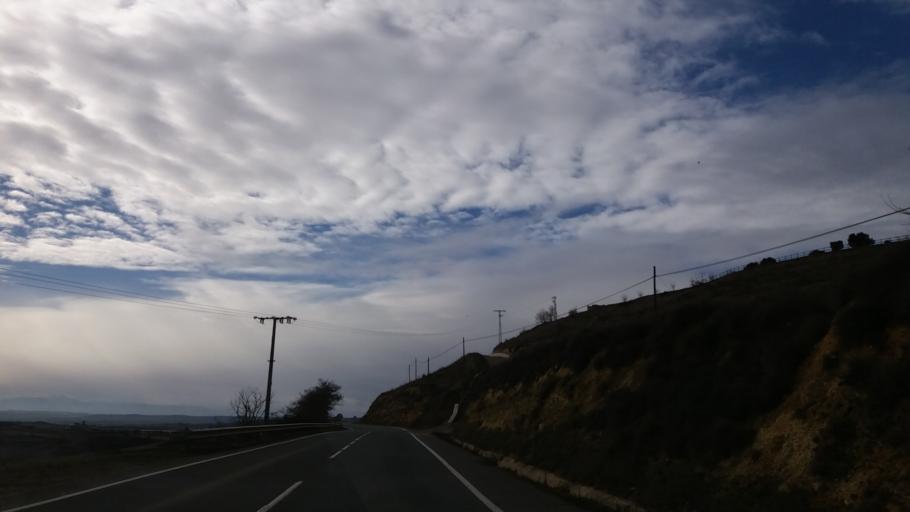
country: ES
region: La Rioja
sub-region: Provincia de La Rioja
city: San Vicente de la Sonsierra
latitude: 42.5527
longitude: -2.7678
